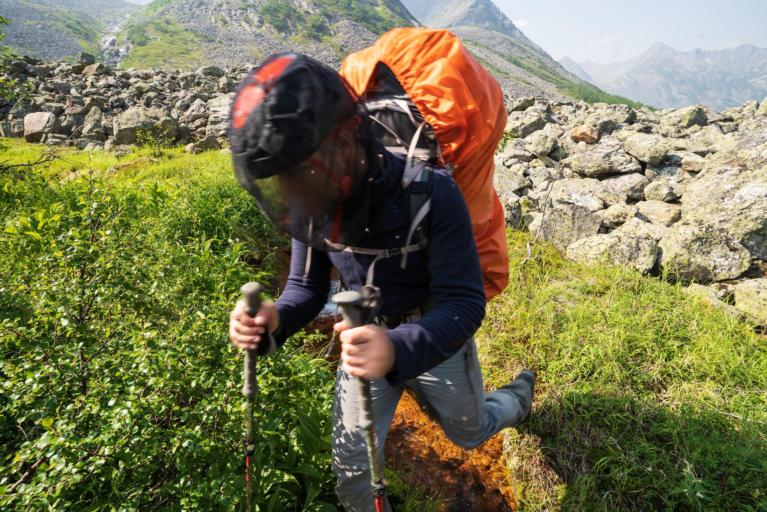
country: RU
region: Transbaikal Territory
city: Kuanda
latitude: 56.8058
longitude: 116.8885
